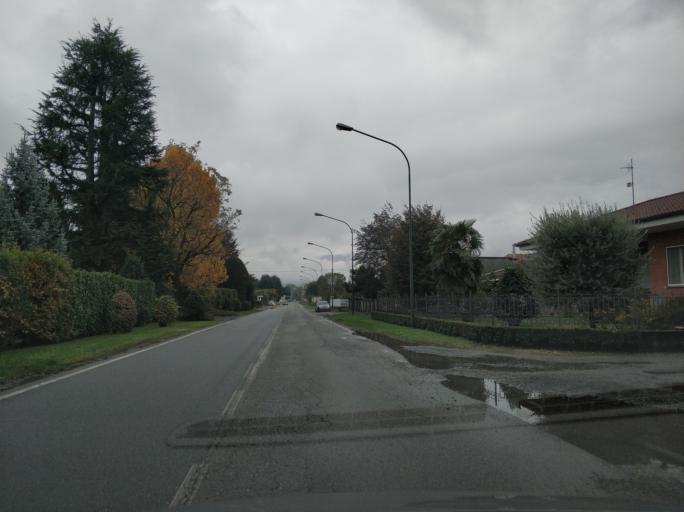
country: IT
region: Piedmont
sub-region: Provincia di Torino
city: Mathi
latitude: 45.2511
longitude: 7.5450
